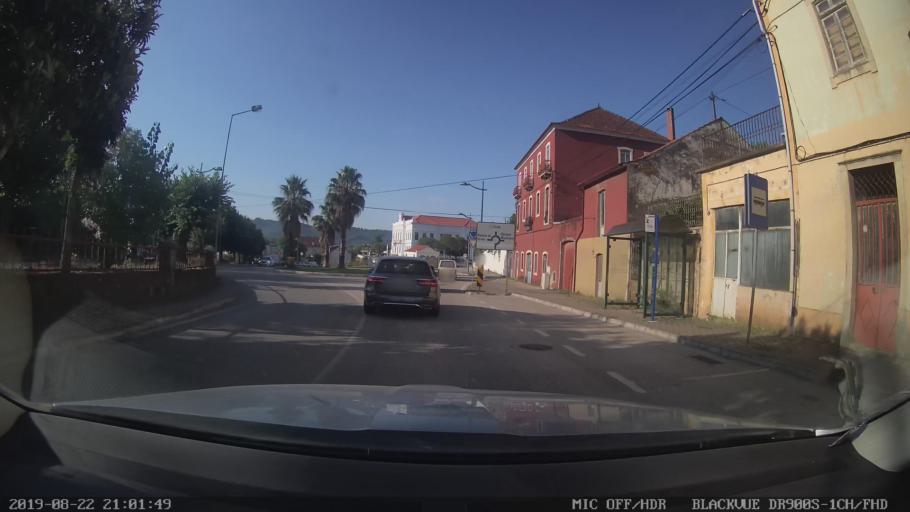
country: PT
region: Castelo Branco
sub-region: Serta
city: Serta
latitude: 39.8109
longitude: -8.0971
